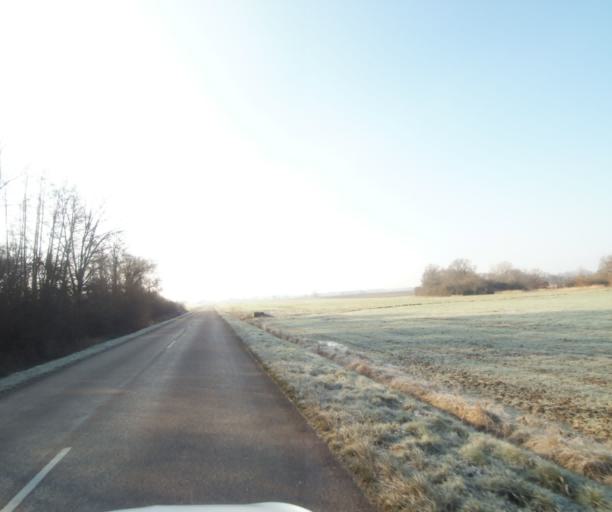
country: FR
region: Champagne-Ardenne
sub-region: Departement de la Haute-Marne
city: Montier-en-Der
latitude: 48.4214
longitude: 4.7457
